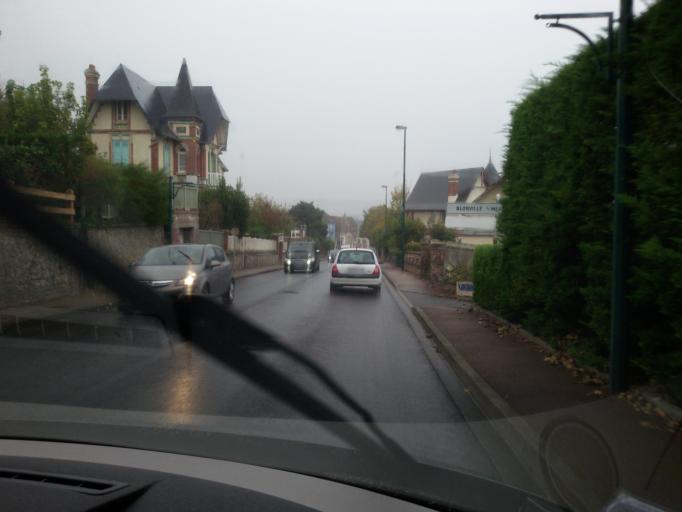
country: FR
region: Lower Normandy
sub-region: Departement du Calvados
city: Blonville-sur-Mer
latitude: 49.3408
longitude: 0.0326
